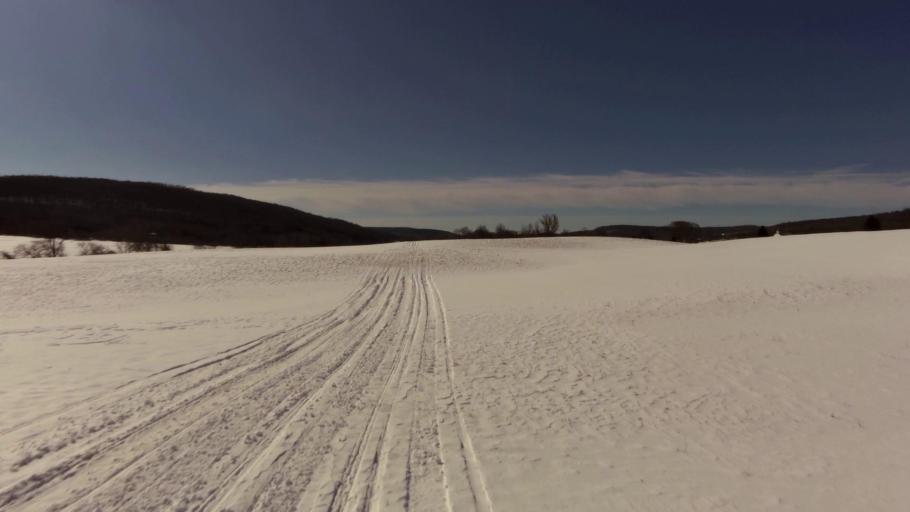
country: US
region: New York
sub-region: Allegany County
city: Cuba
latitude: 42.3353
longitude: -78.3060
